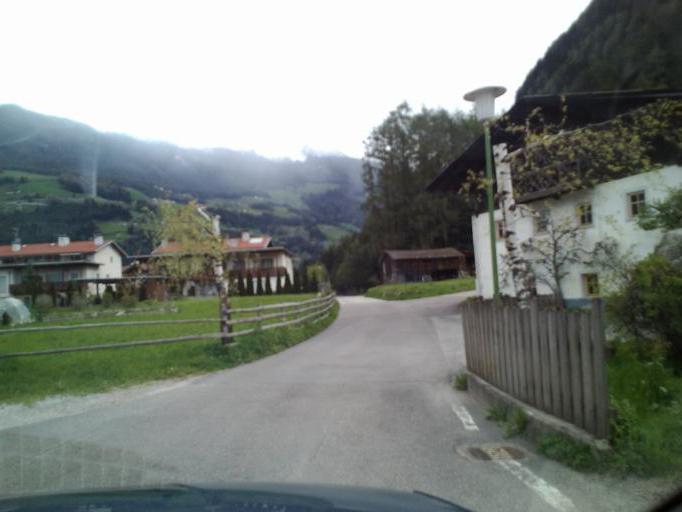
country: IT
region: Trentino-Alto Adige
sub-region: Bolzano
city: Campo Tures
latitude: 46.9041
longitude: 11.9581
